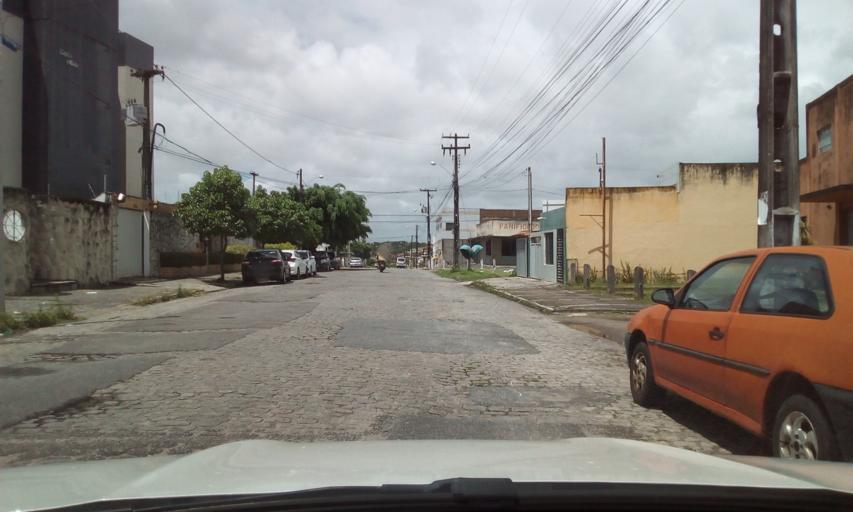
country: BR
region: Paraiba
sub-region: Joao Pessoa
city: Joao Pessoa
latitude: -7.1364
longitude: -34.8775
